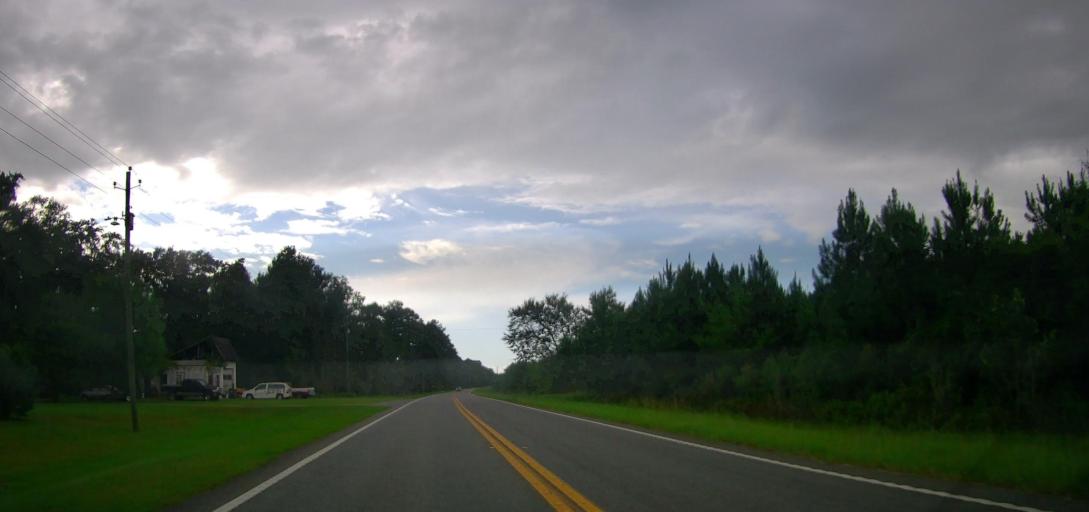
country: US
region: Georgia
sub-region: Ware County
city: Deenwood
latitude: 31.2876
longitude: -82.5500
